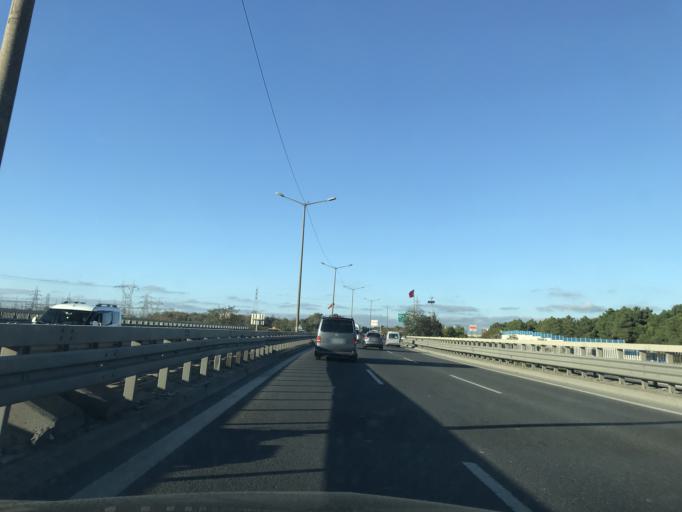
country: TR
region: Istanbul
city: Sisli
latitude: 41.0896
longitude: 28.9609
